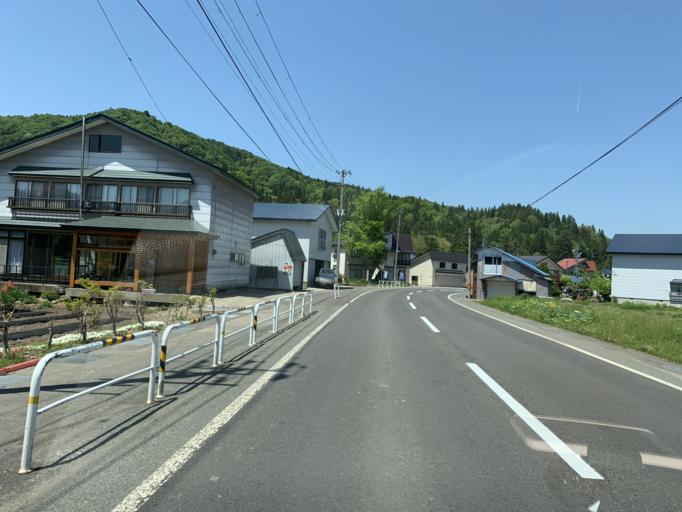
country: JP
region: Akita
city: Yokotemachi
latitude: 39.4221
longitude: 140.7451
